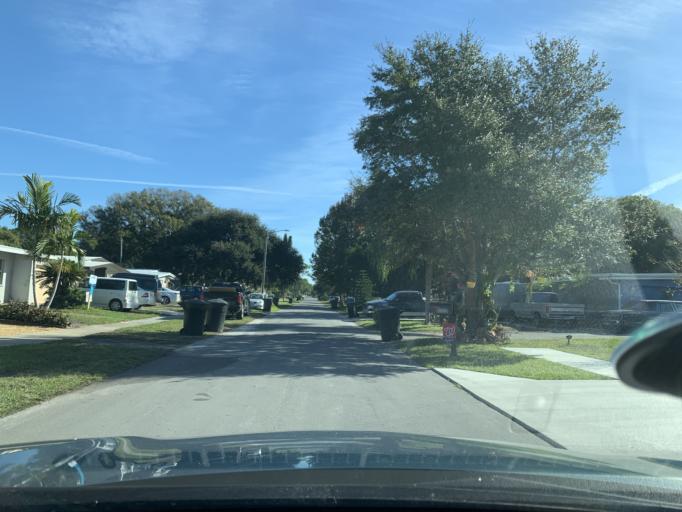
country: US
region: Florida
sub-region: Pinellas County
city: Gulfport
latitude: 27.7563
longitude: -82.7063
